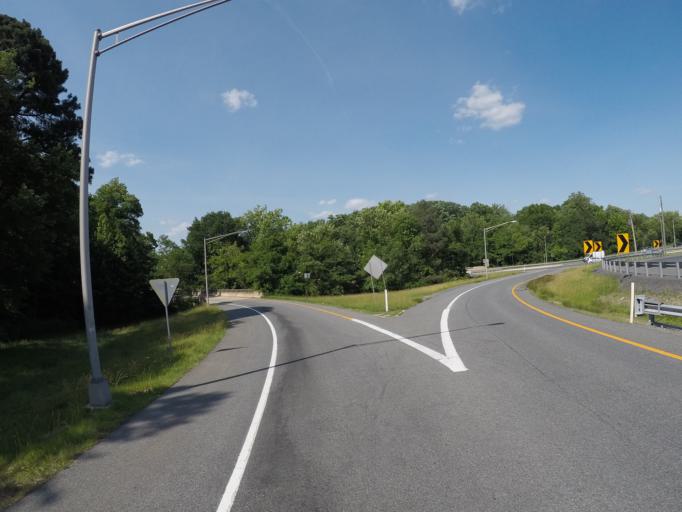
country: US
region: Delaware
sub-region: New Castle County
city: Brookside
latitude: 39.6484
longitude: -75.7485
